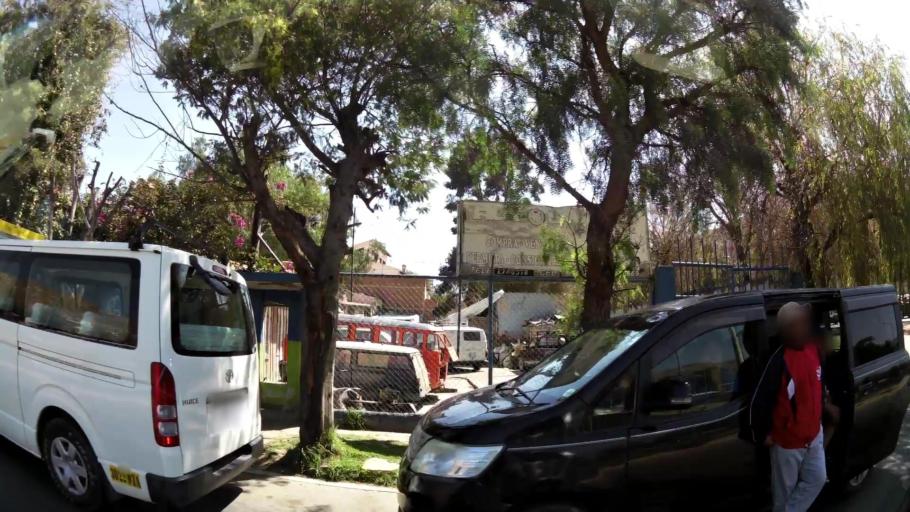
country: BO
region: La Paz
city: La Paz
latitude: -16.5420
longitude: -68.0944
